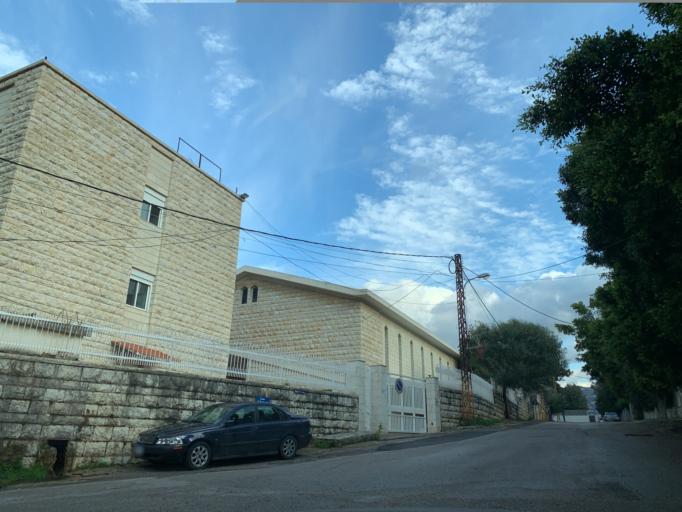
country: LB
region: Mont-Liban
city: Baabda
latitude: 33.8518
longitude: 35.5782
